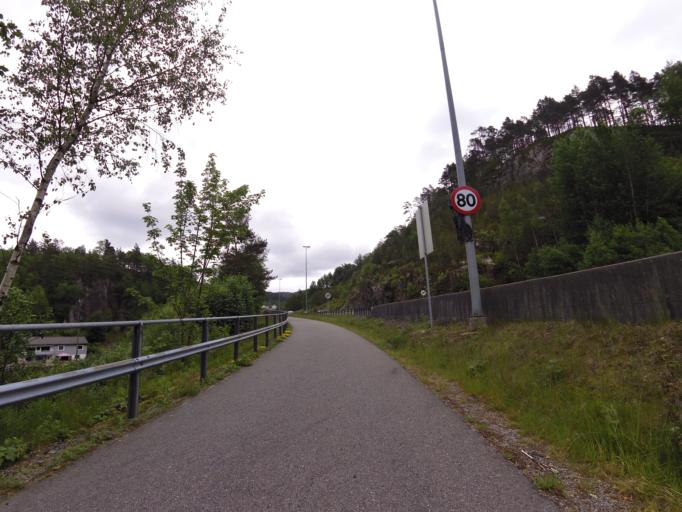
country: NO
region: Vest-Agder
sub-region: Flekkefjord
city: Flekkefjord
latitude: 58.2958
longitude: 6.6825
